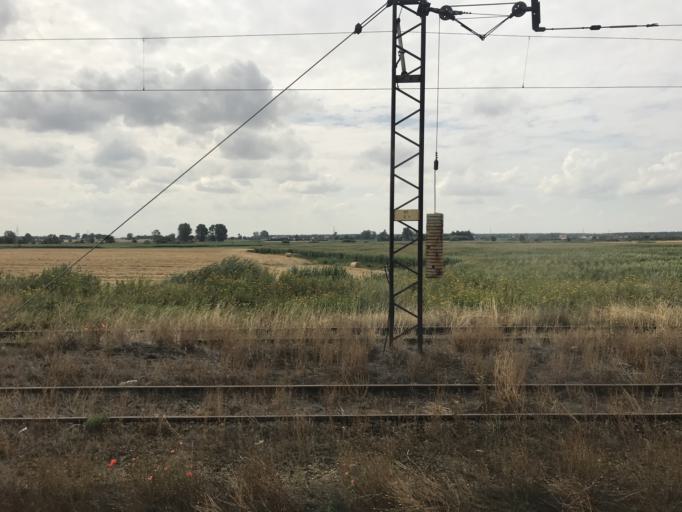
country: PL
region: Greater Poland Voivodeship
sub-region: Powiat gnieznienski
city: Gniezno
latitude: 52.5326
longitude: 17.6473
